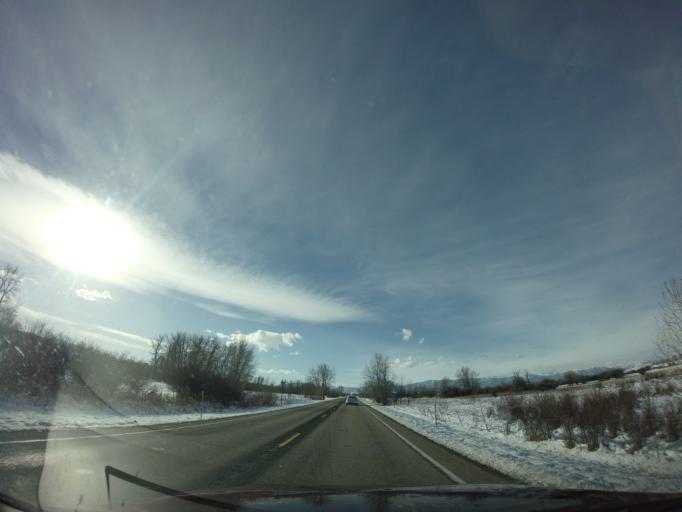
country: US
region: Montana
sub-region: Carbon County
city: Red Lodge
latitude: 45.3415
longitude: -109.1791
